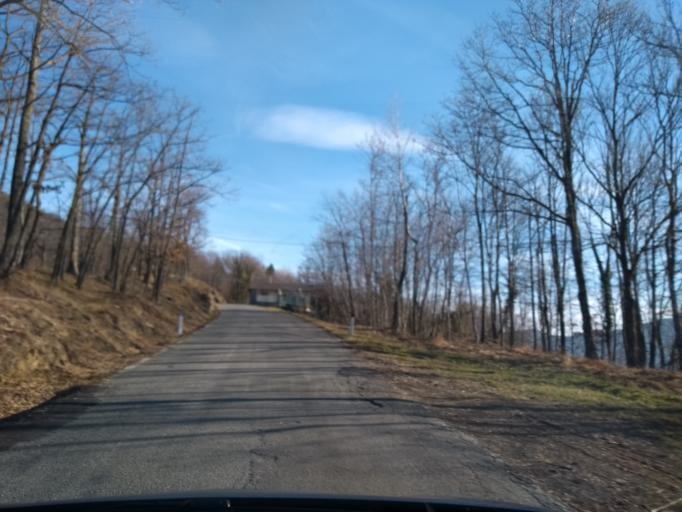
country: IT
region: Piedmont
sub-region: Provincia di Torino
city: Pessinetto
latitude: 45.2847
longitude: 7.4272
